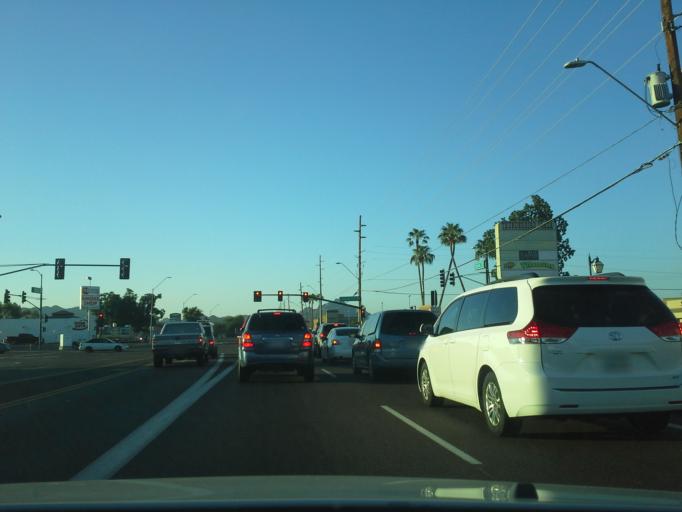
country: US
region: Arizona
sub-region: Maricopa County
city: Paradise Valley
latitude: 33.6122
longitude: -112.0133
